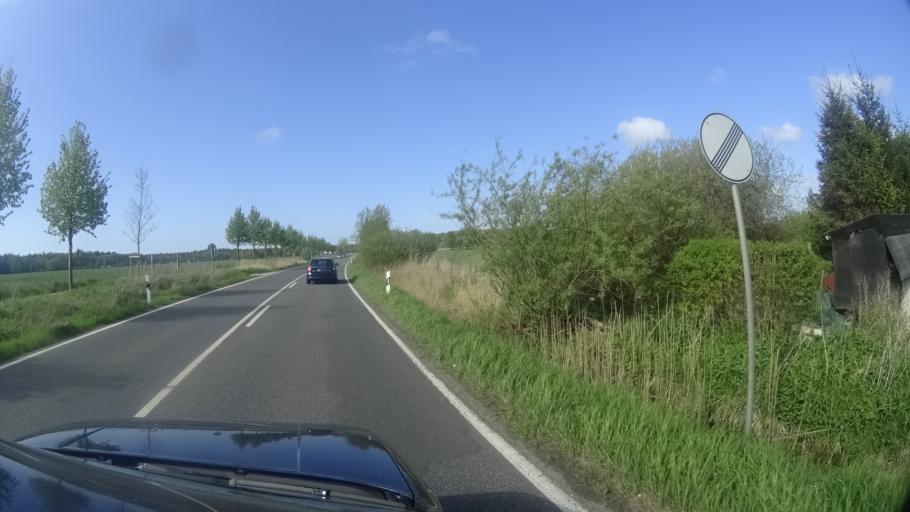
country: DE
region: Mecklenburg-Vorpommern
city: Monchhagen
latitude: 54.1802
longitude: 12.2053
